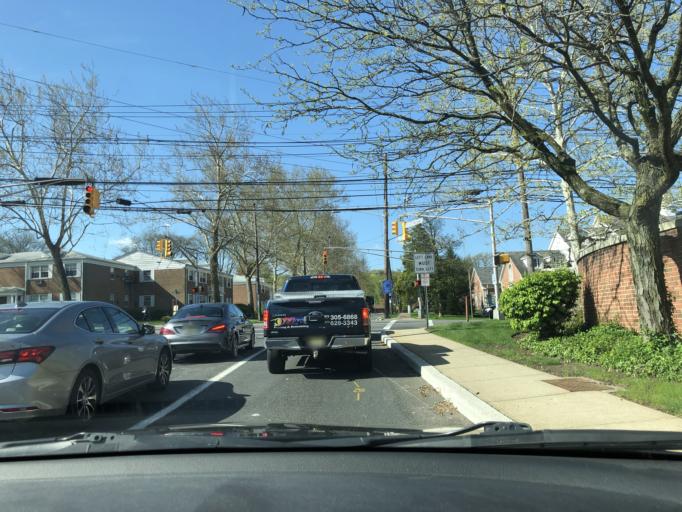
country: US
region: New Jersey
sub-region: Passaic County
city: Singac
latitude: 40.8831
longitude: -74.2334
